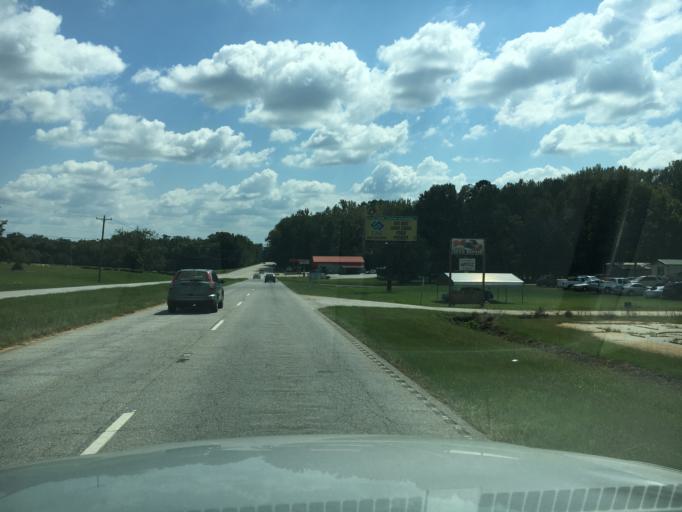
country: US
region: South Carolina
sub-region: Greenwood County
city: Greenwood
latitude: 34.2625
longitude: -82.2257
